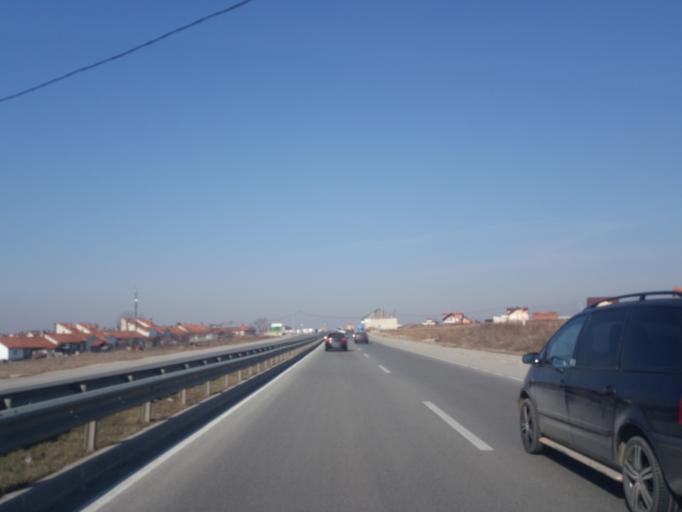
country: XK
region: Pristina
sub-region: Komuna e Obiliqit
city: Obiliq
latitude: 42.7570
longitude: 21.0345
